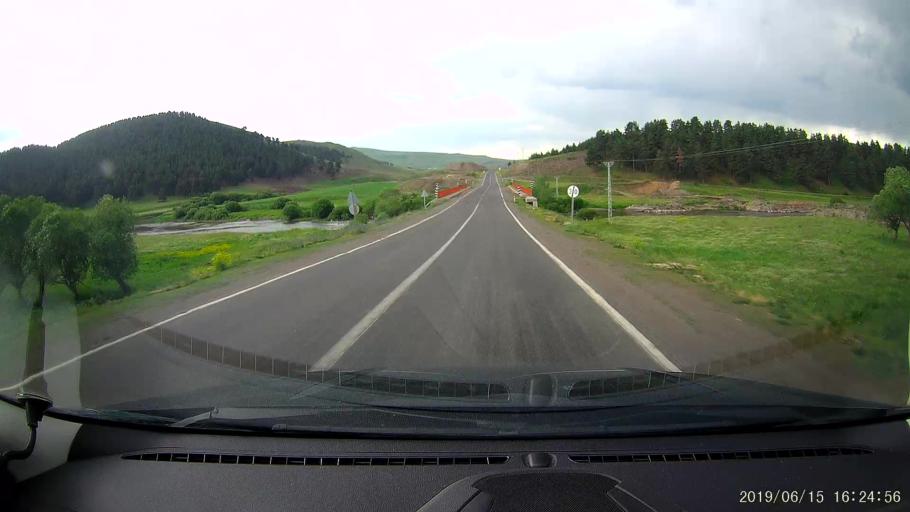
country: TR
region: Ardahan
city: Hanak
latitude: 41.1606
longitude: 42.8721
